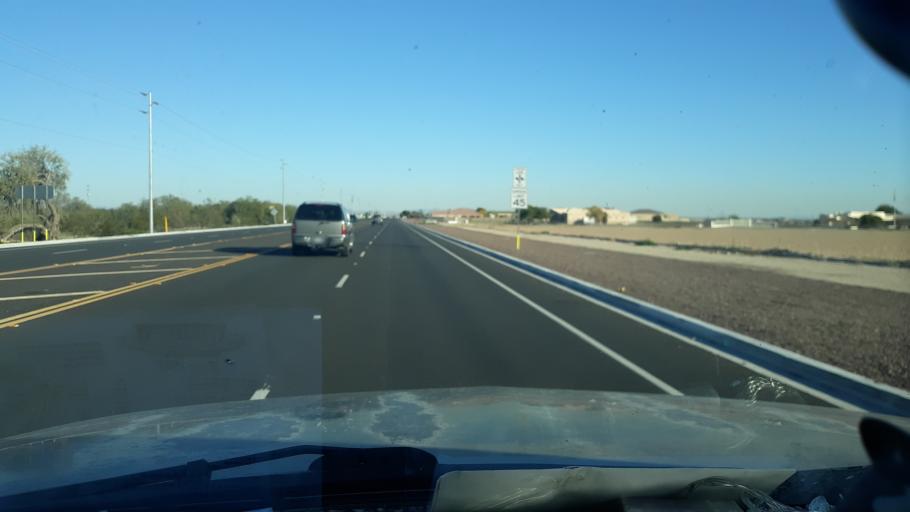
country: US
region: Arizona
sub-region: Maricopa County
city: Citrus Park
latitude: 33.5662
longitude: -112.4422
